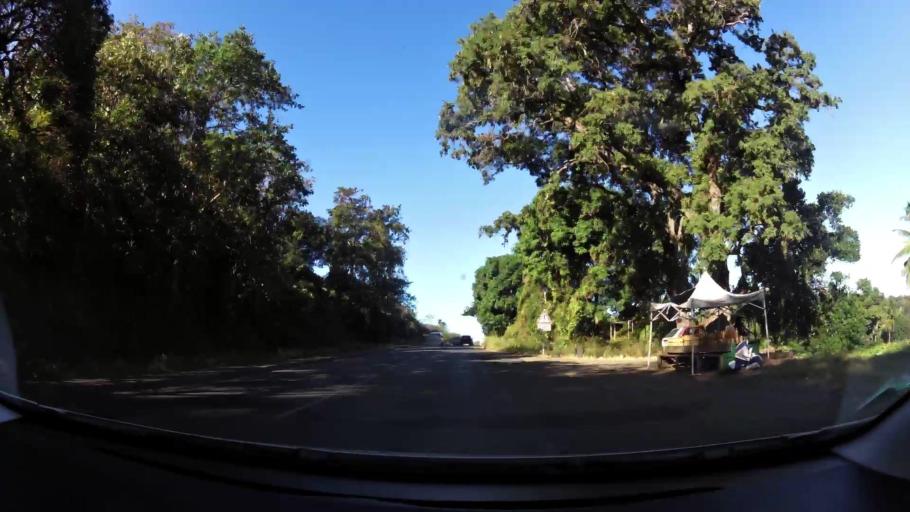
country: YT
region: Mamoudzou
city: Mamoudzou
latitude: -12.7594
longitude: 45.2288
